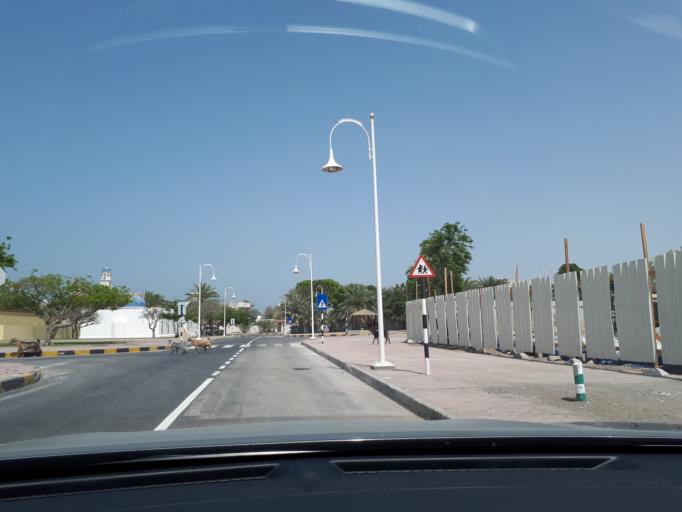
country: OM
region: Muhafazat Masqat
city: As Sib al Jadidah
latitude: 23.7114
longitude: 58.0733
